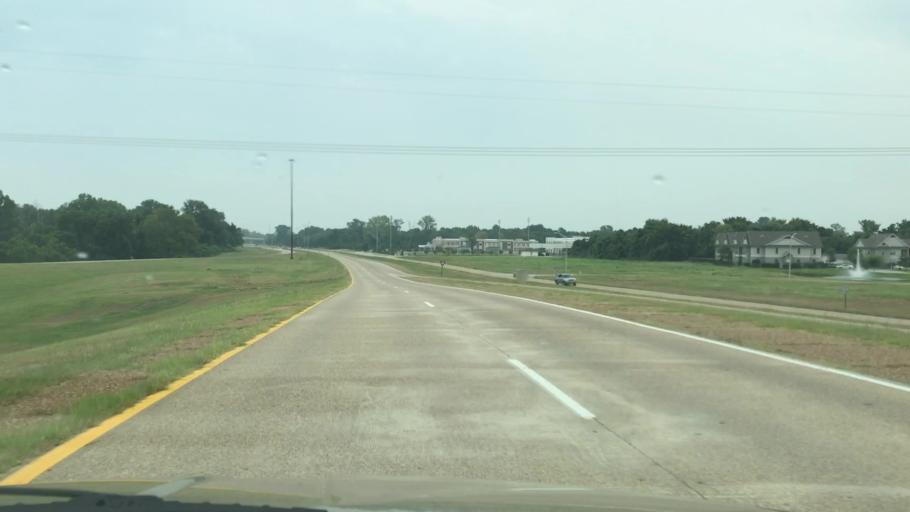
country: US
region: Louisiana
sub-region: Bossier Parish
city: Bossier City
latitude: 32.4998
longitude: -93.7152
